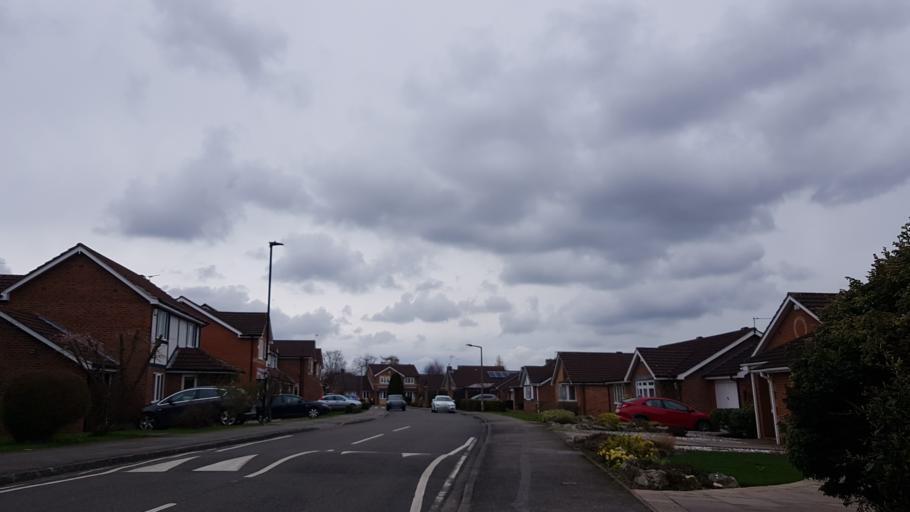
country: GB
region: England
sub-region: City of York
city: Huntington
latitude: 53.9891
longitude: -1.0621
